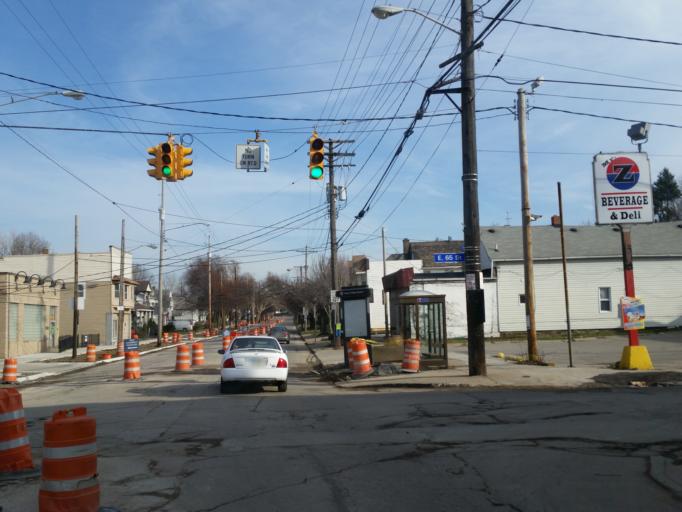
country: US
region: Ohio
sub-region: Cuyahoga County
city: Newburgh Heights
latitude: 41.4561
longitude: -81.6450
